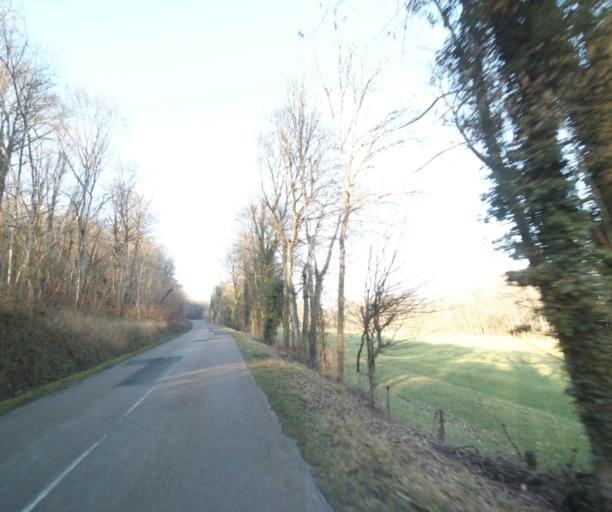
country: FR
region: Champagne-Ardenne
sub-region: Departement de la Haute-Marne
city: Bienville
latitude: 48.5667
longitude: 5.0797
